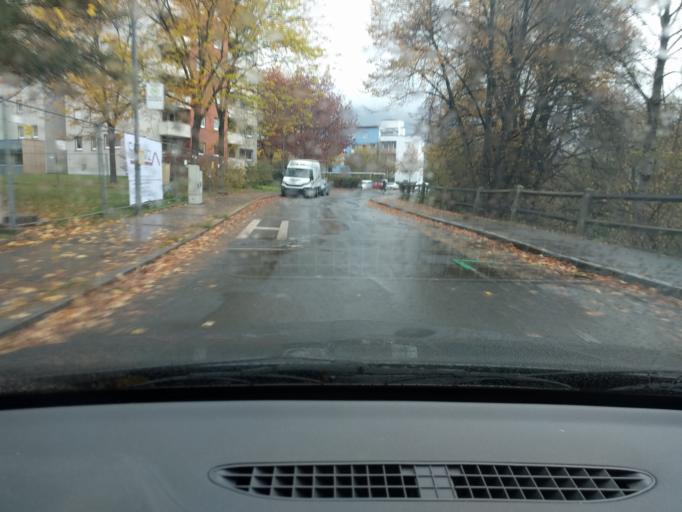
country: AT
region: Styria
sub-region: Politischer Bezirk Leoben
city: Leoben
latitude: 47.3823
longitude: 15.1034
